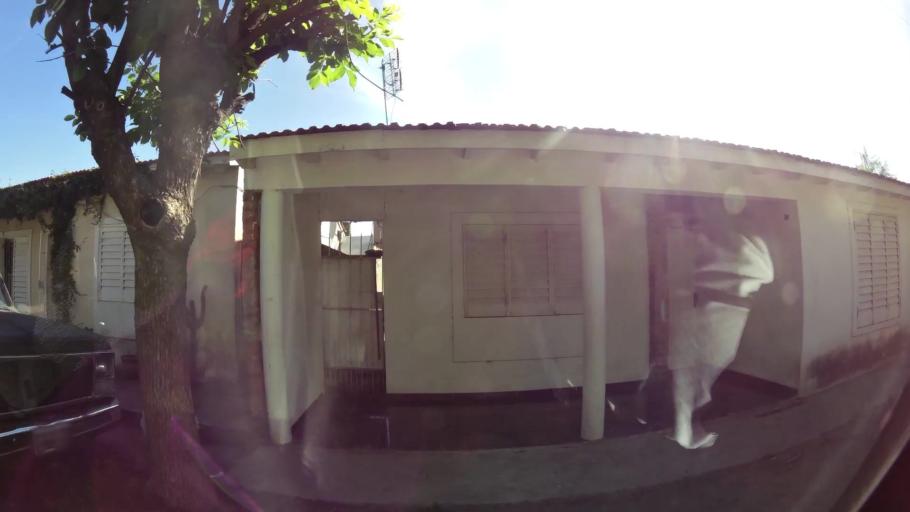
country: AR
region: Buenos Aires
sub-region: Partido de Almirante Brown
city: Adrogue
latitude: -34.8274
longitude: -58.3525
